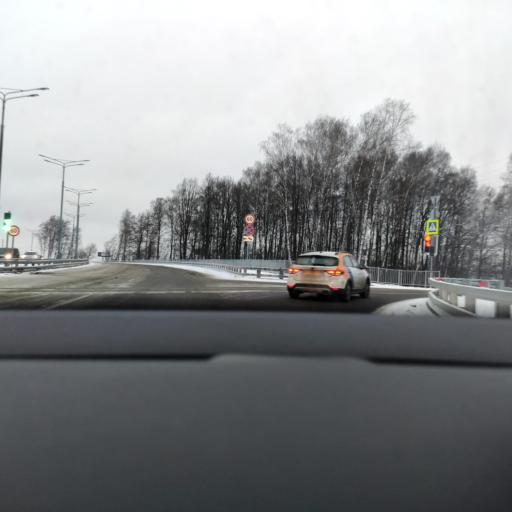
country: RU
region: Moscow
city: Tyoply Stan
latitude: 55.6007
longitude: 37.4889
